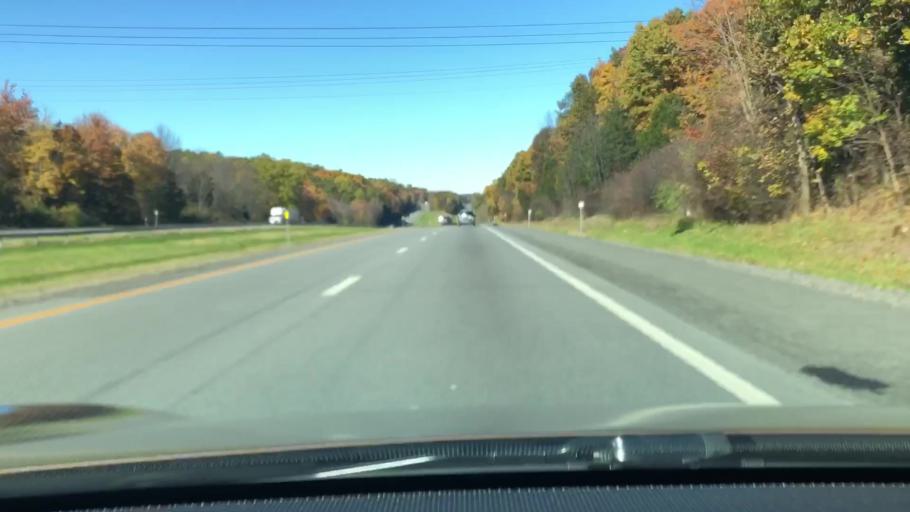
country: US
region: New York
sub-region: Orange County
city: Vails Gate
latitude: 41.4640
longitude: -74.0689
